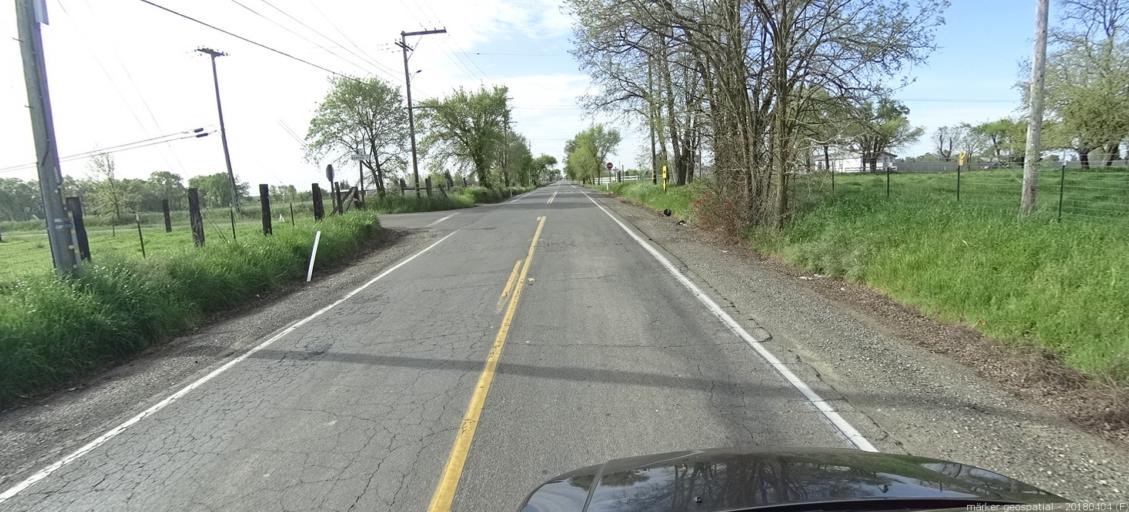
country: US
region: California
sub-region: Sacramento County
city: Herald
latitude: 38.2925
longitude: -121.2265
